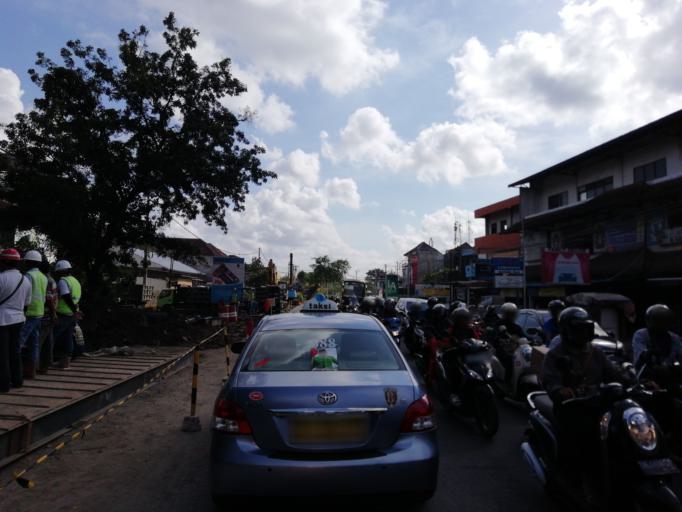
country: ID
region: Bali
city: Kuta
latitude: -8.6979
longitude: 115.1857
